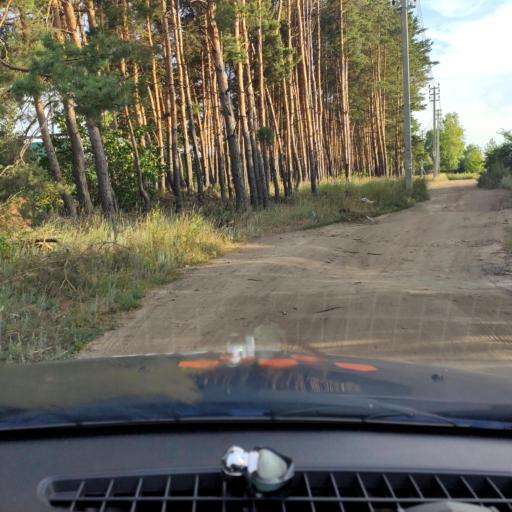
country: RU
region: Voronezj
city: Podgornoye
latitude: 51.8504
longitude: 39.1526
